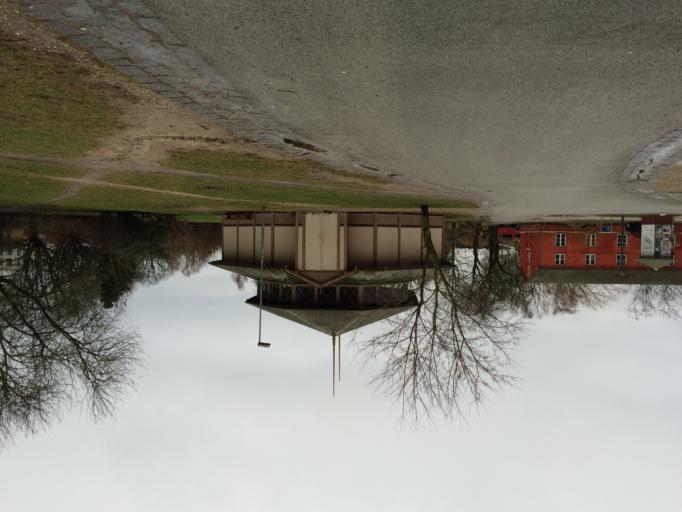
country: DK
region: Capital Region
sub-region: Frederiksberg Kommune
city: Frederiksberg
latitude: 55.6468
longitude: 12.5293
